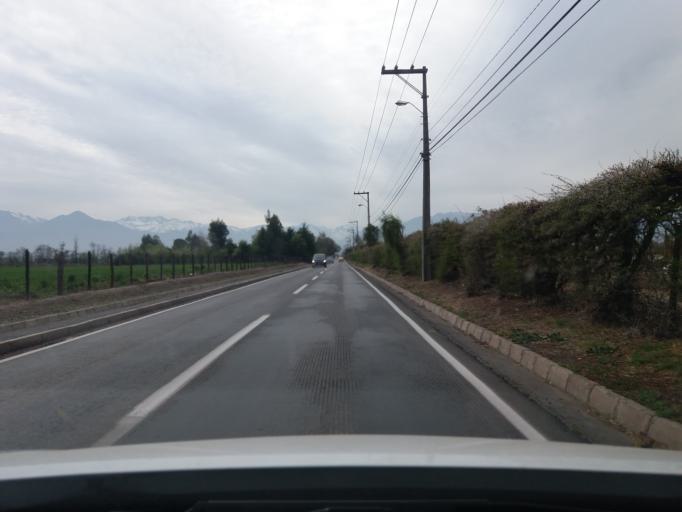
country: CL
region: Valparaiso
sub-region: Provincia de Los Andes
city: Los Andes
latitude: -32.8200
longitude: -70.6786
